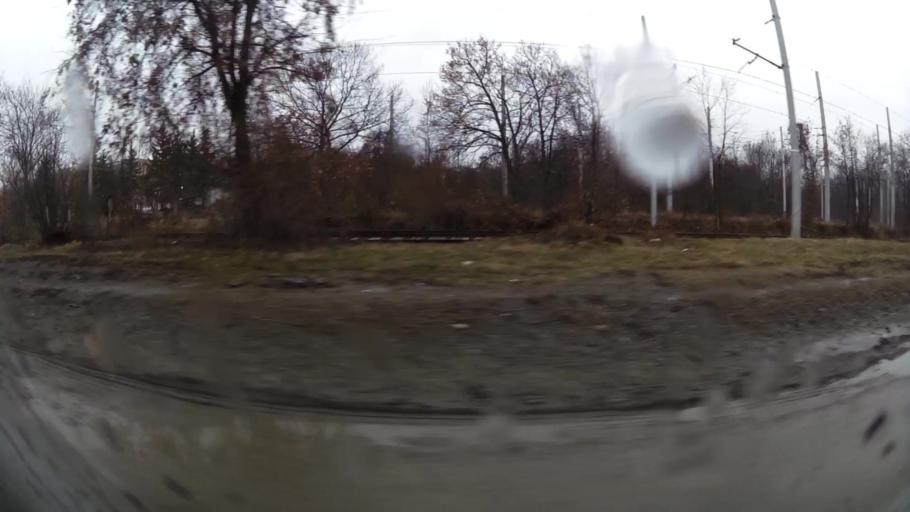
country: BG
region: Sofia-Capital
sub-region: Stolichna Obshtina
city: Sofia
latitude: 42.6635
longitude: 23.4130
